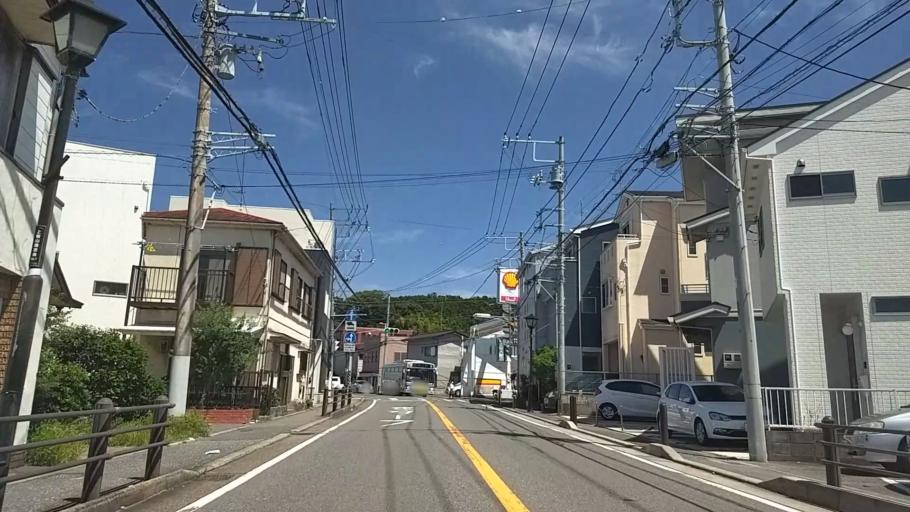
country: JP
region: Kanagawa
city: Zushi
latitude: 35.2952
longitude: 139.5864
